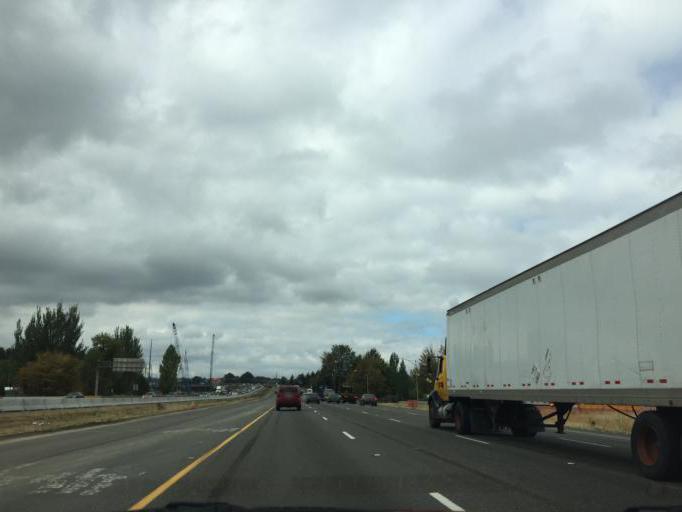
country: US
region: Washington
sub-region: Pierce County
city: Fife
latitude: 47.2415
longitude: -122.3875
